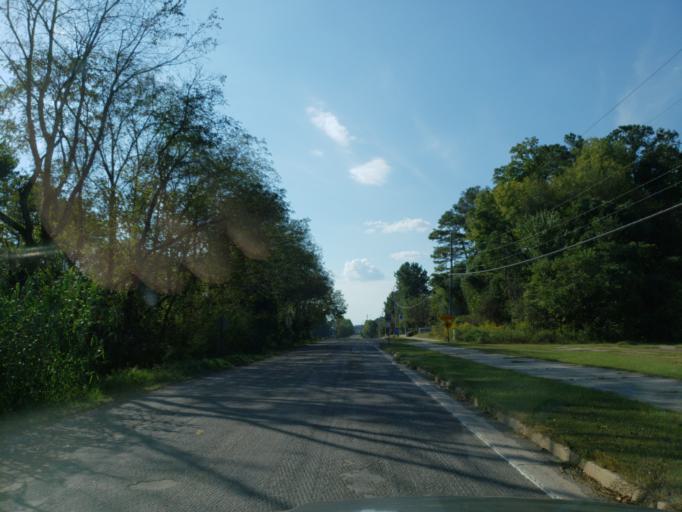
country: US
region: Georgia
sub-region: Cobb County
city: Powder Springs
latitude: 33.8625
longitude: -84.6892
